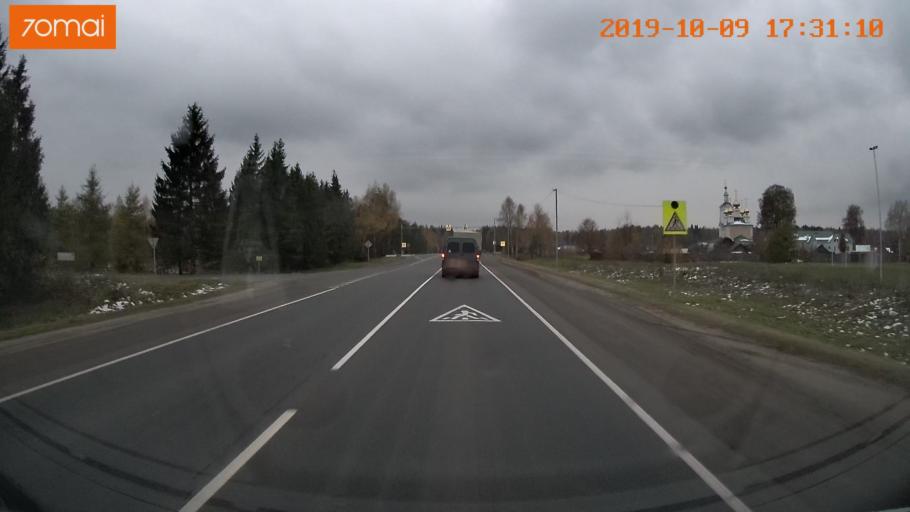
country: RU
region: Ivanovo
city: Bogorodskoye
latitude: 57.1375
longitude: 41.0420
